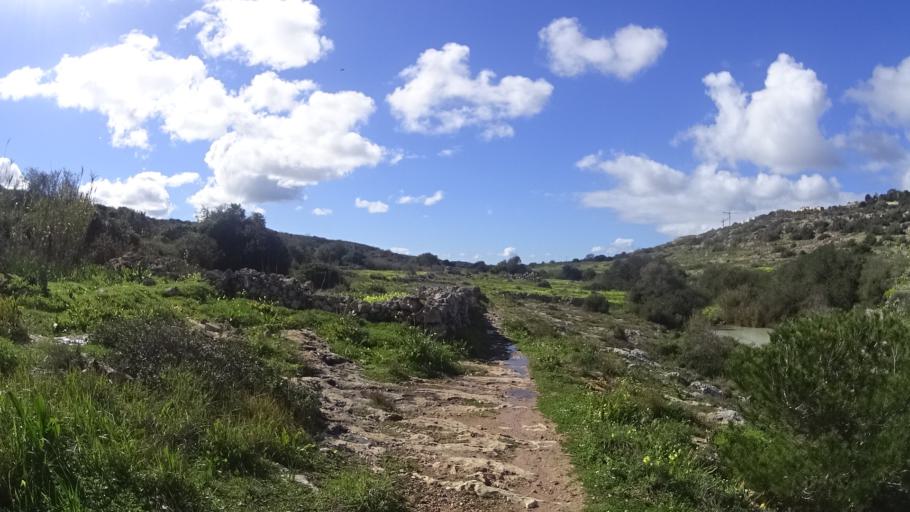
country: MT
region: Il-Mellieha
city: Mellieha
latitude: 35.9520
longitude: 14.3793
